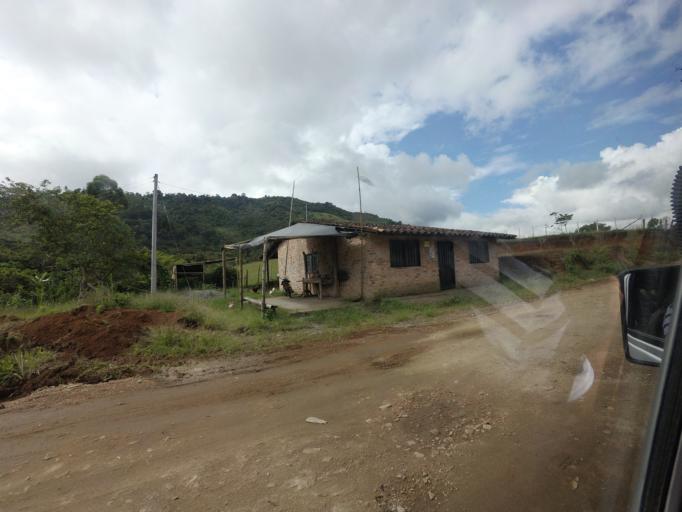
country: CO
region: Huila
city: San Agustin
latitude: 1.9235
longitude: -76.2927
